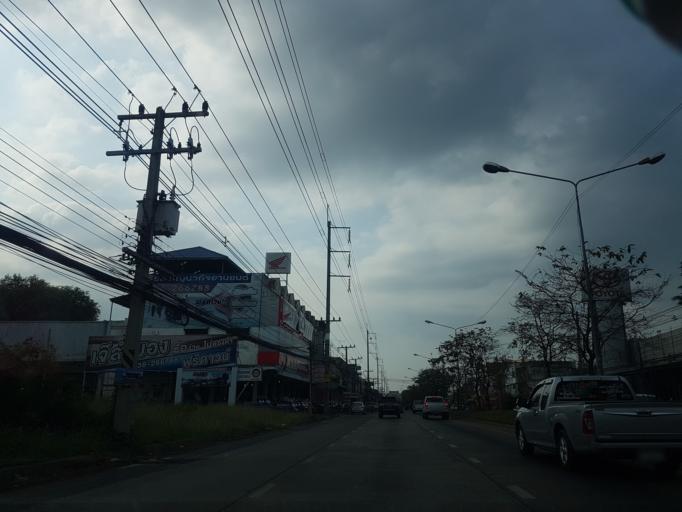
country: TH
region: Sara Buri
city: Phra Phutthabat
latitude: 14.7292
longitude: 100.7892
